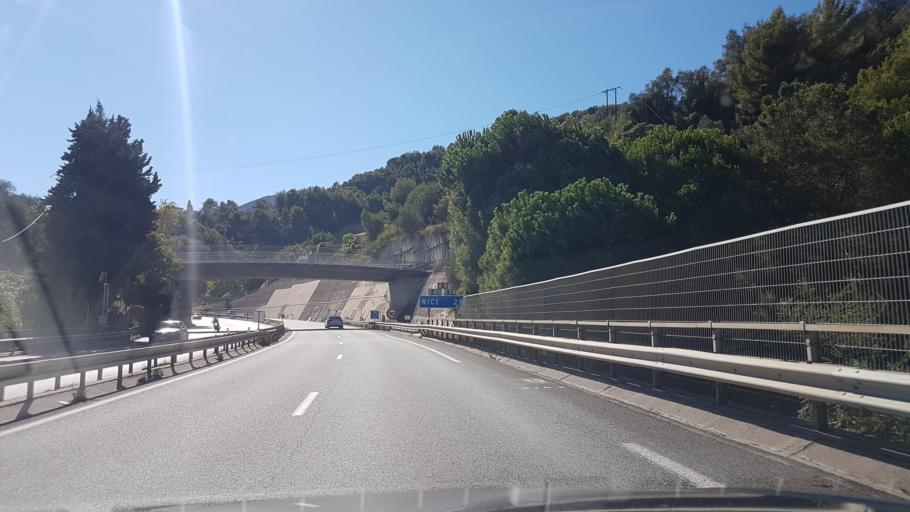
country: FR
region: Provence-Alpes-Cote d'Azur
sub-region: Departement des Alpes-Maritimes
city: Sainte-Agnes
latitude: 43.7966
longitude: 7.4783
